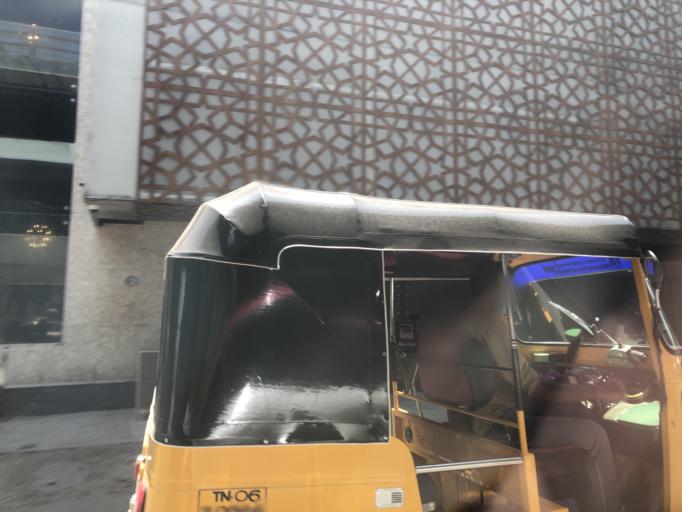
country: IN
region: Tamil Nadu
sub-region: Chennai
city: Gandhi Nagar
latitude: 13.0381
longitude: 80.2565
